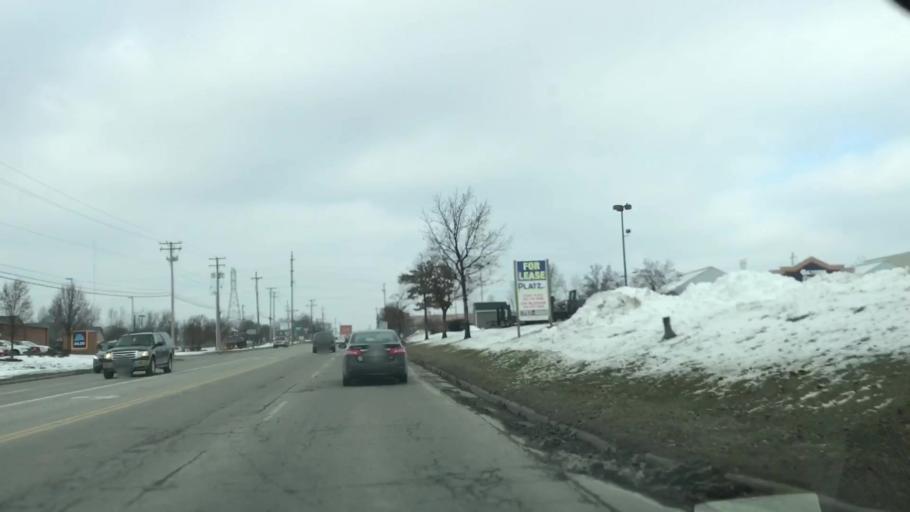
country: US
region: Ohio
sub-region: Mahoning County
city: Poland
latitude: 41.0303
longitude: -80.6345
